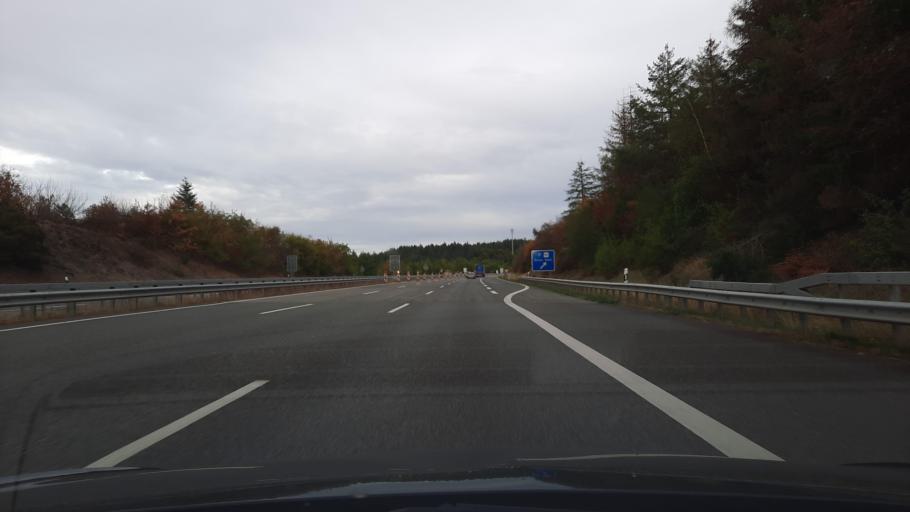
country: DE
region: Rheinland-Pfalz
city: Mehring
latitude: 49.7844
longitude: 6.8124
